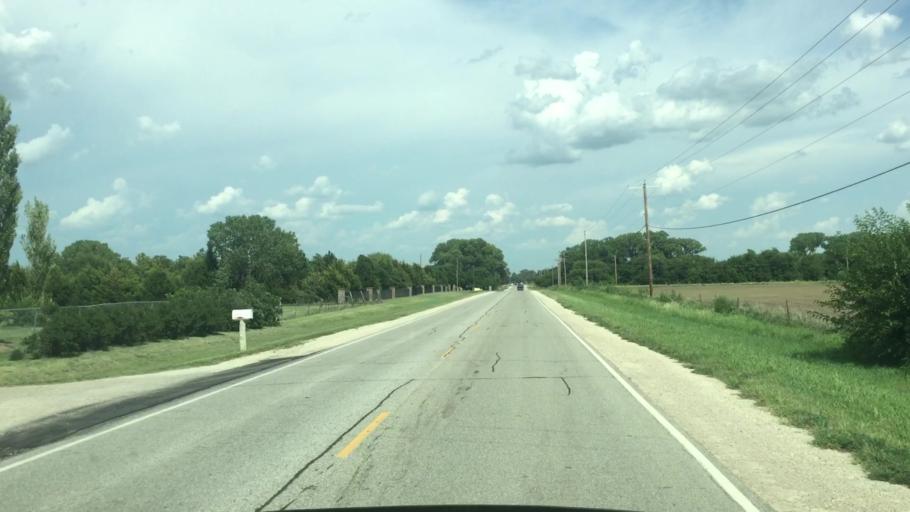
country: US
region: Kansas
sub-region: Sedgwick County
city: Maize
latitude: 37.7811
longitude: -97.4393
